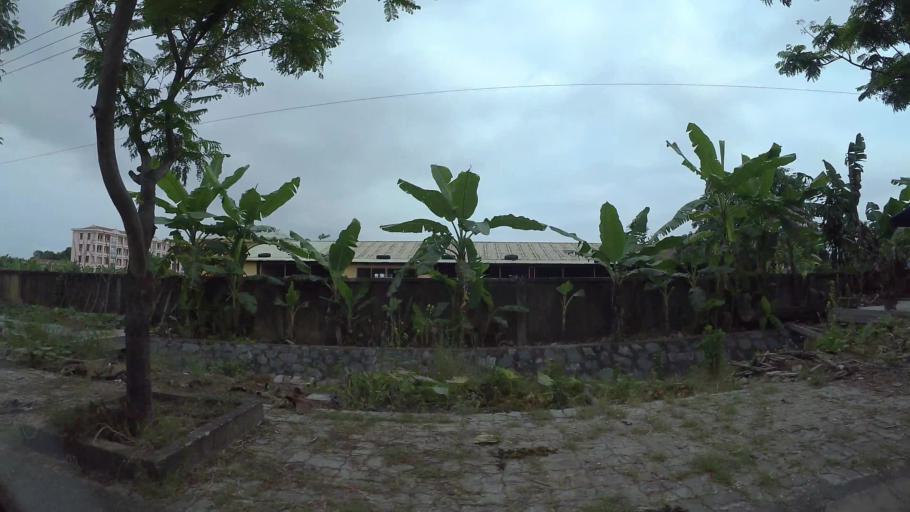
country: VN
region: Da Nang
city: Cam Le
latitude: 16.0351
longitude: 108.1754
